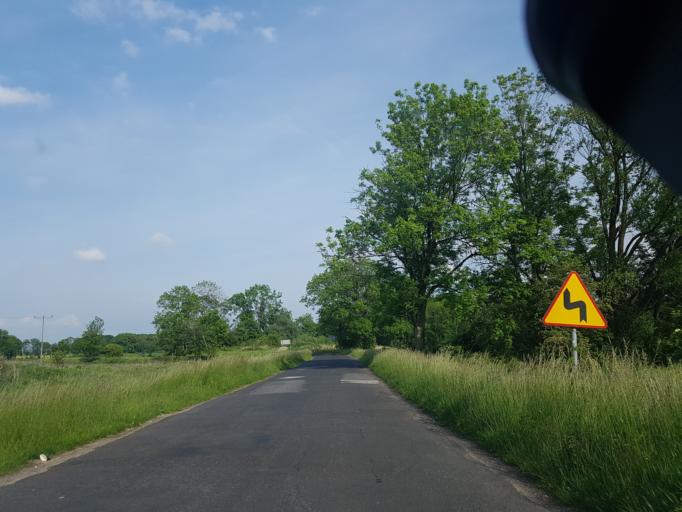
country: PL
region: Lower Silesian Voivodeship
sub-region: Powiat wroclawski
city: Zorawina
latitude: 50.9095
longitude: 17.0770
